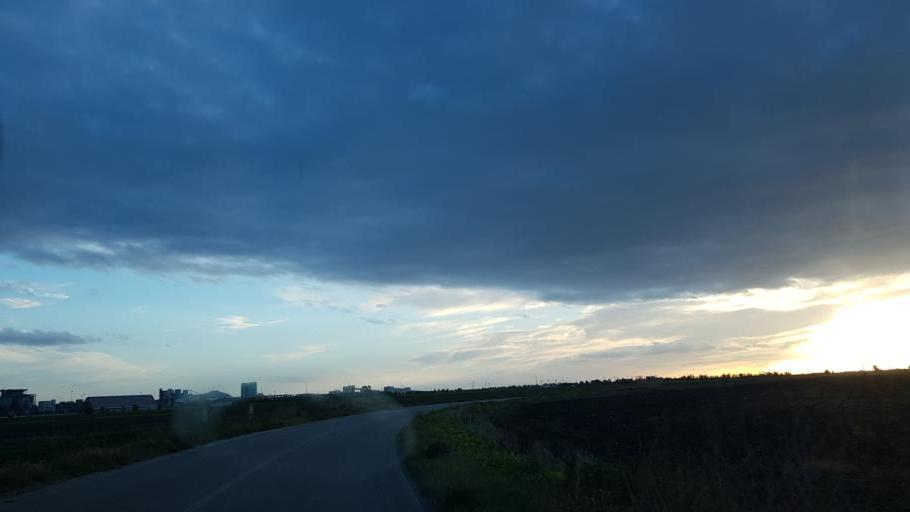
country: IT
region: Apulia
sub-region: Provincia di Brindisi
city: La Rosa
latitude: 40.5824
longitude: 18.0331
